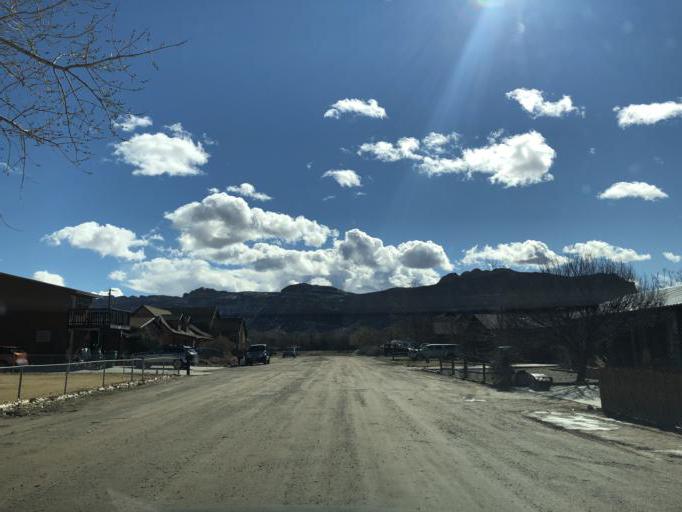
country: US
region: Utah
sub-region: Grand County
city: Moab
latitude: 38.5873
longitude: -109.5650
